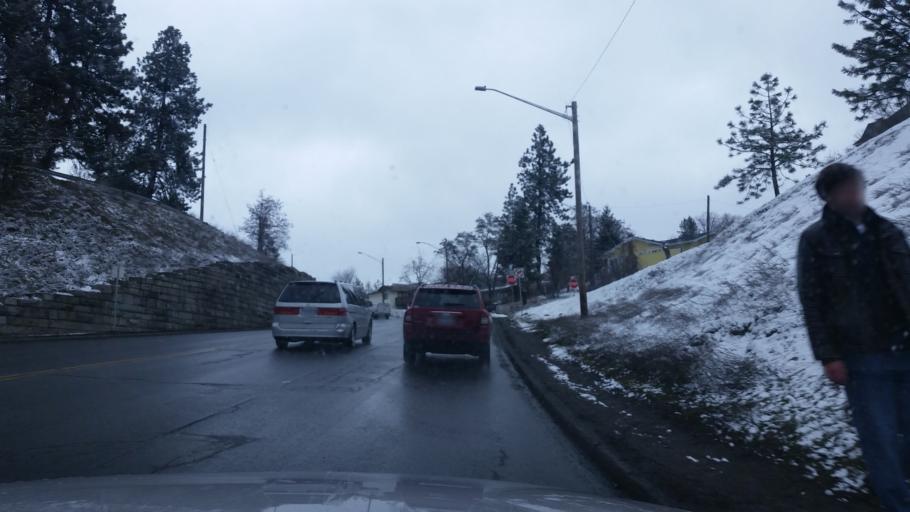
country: US
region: Washington
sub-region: Spokane County
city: Spokane
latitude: 47.6901
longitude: -117.4265
